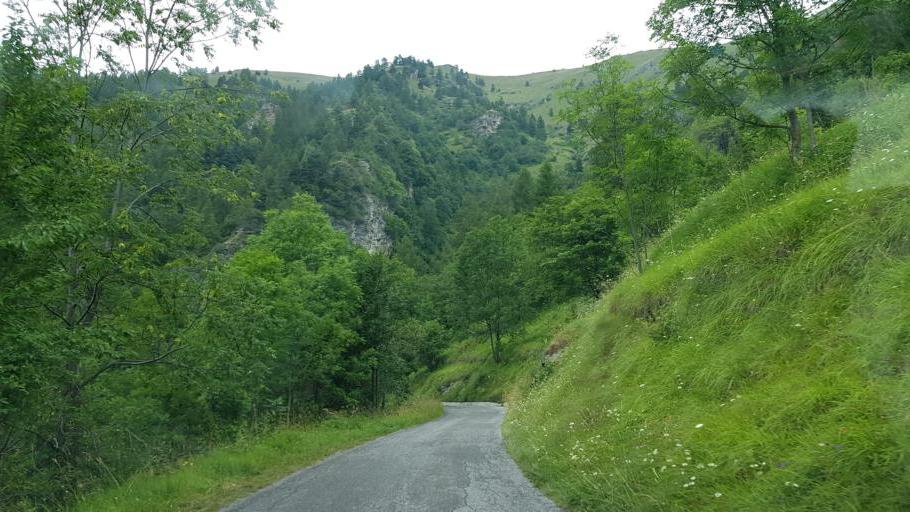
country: IT
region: Piedmont
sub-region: Provincia di Cuneo
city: Stroppo
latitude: 44.5194
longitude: 7.1183
